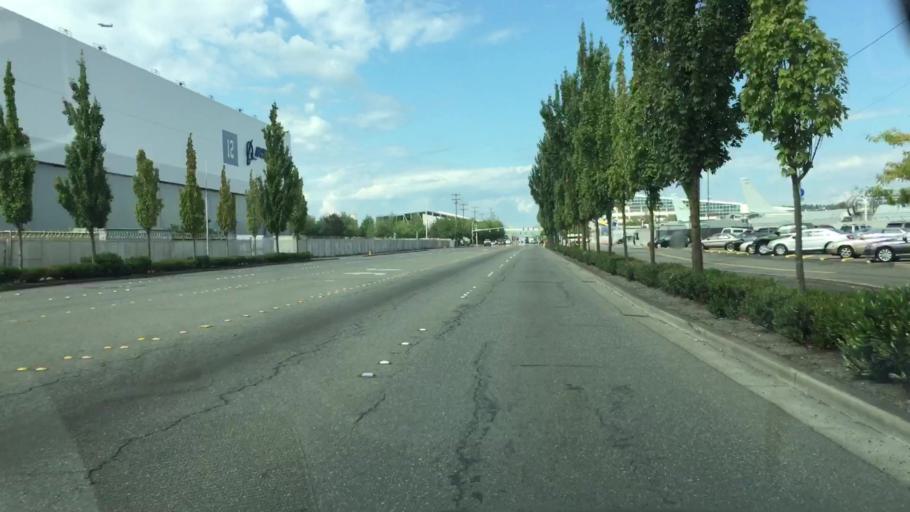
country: US
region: Washington
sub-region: King County
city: Riverton
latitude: 47.5139
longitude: -122.2948
